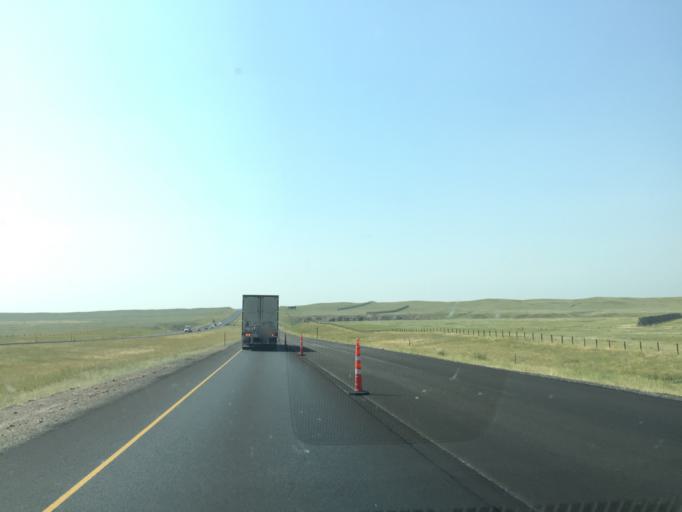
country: US
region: Wyoming
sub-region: Laramie County
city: Ranchettes
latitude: 41.3304
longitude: -104.8639
